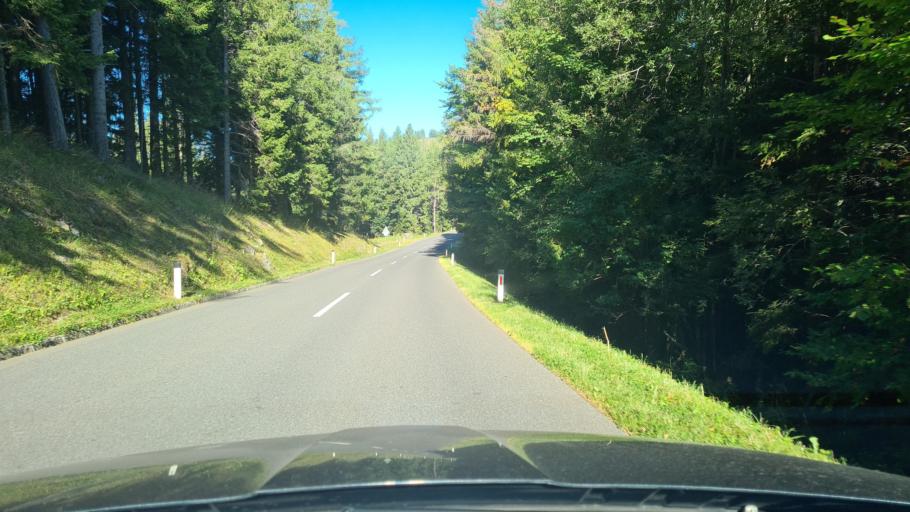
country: AT
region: Styria
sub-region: Politischer Bezirk Weiz
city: Passail
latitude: 47.3261
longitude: 15.4772
